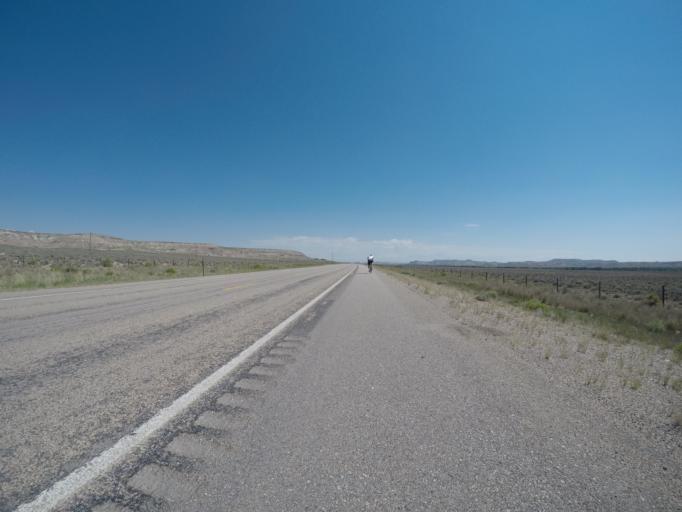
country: US
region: Wyoming
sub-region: Sublette County
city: Marbleton
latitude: 42.3805
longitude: -110.1390
